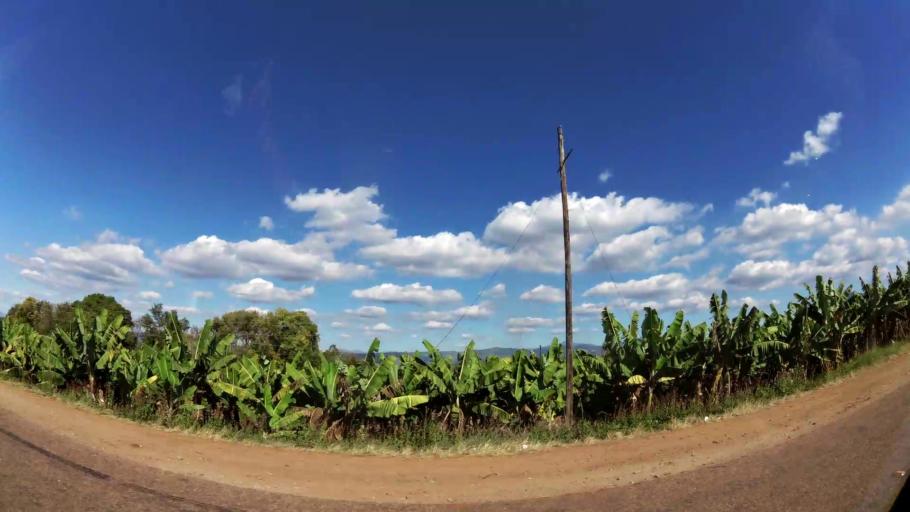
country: ZA
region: Limpopo
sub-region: Mopani District Municipality
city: Tzaneen
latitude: -23.8027
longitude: 30.1216
